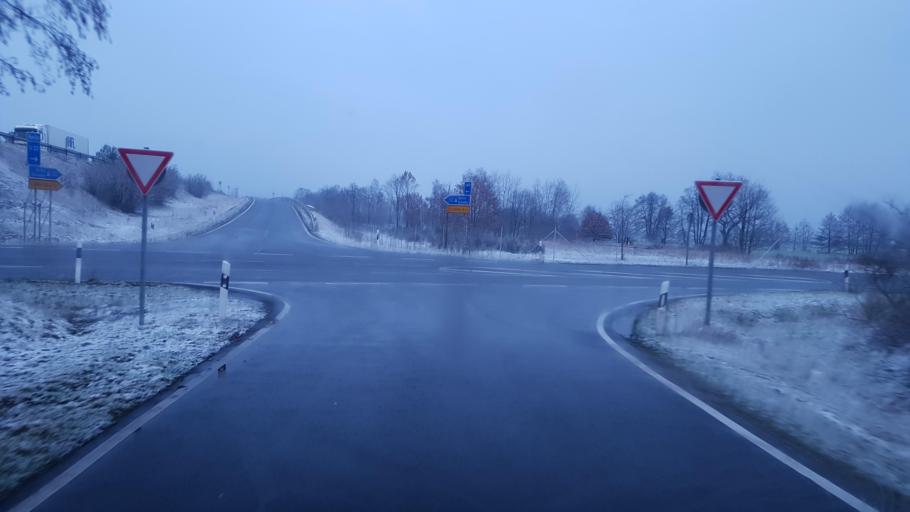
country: DE
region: Brandenburg
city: Luckau
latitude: 51.8641
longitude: 13.7335
